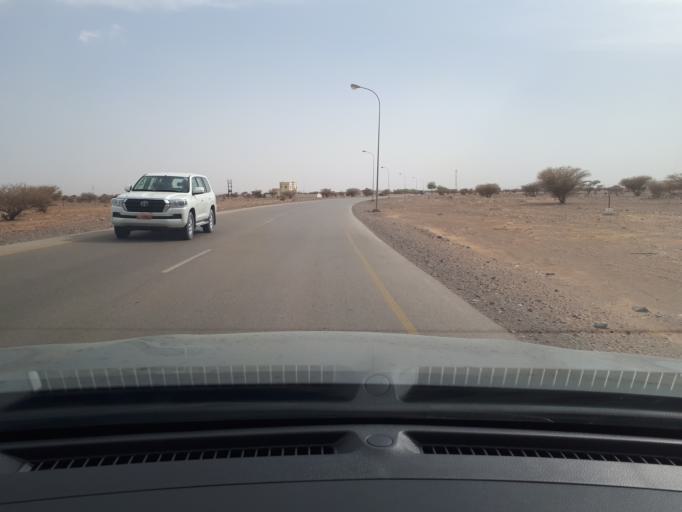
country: OM
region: Ash Sharqiyah
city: Badiyah
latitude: 22.5035
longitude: 58.9460
